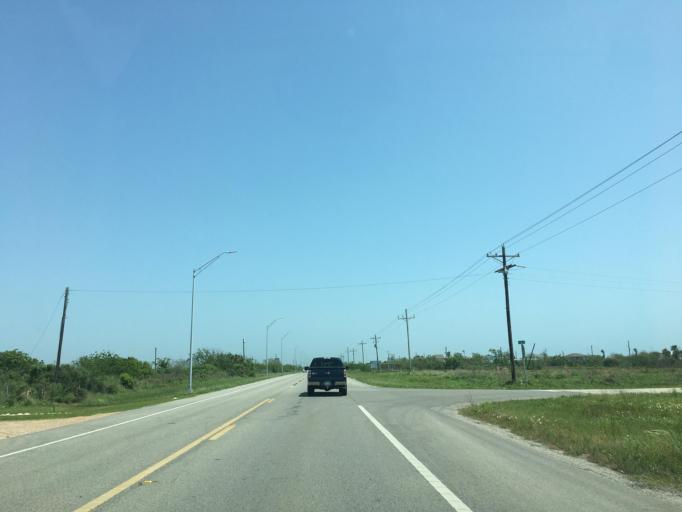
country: US
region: Texas
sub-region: Galveston County
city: Galveston
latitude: 29.3734
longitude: -94.7537
